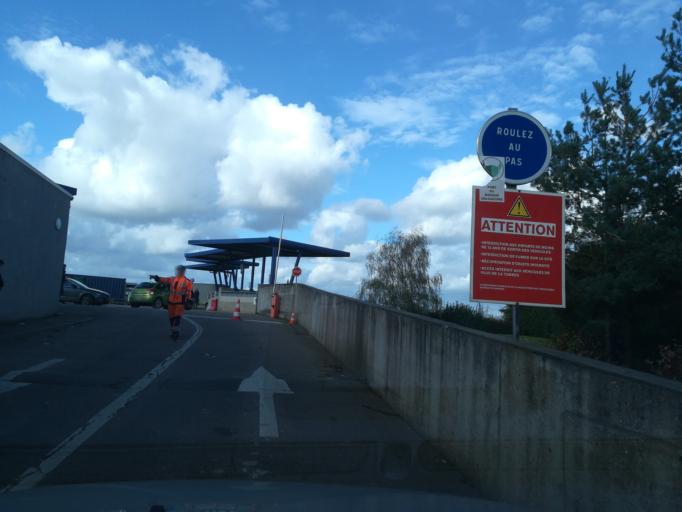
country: FR
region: Haute-Normandie
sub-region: Departement de la Seine-Maritime
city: Bois-Guillaume
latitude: 49.4756
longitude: 1.1359
